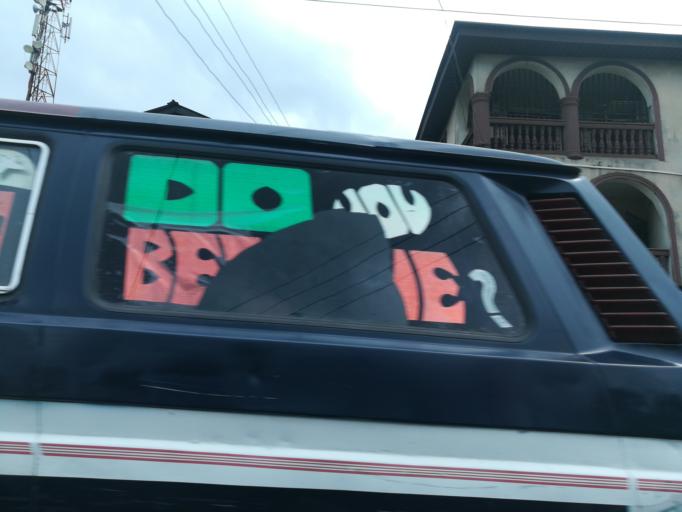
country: NG
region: Rivers
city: Port Harcourt
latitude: 4.7564
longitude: 7.0370
